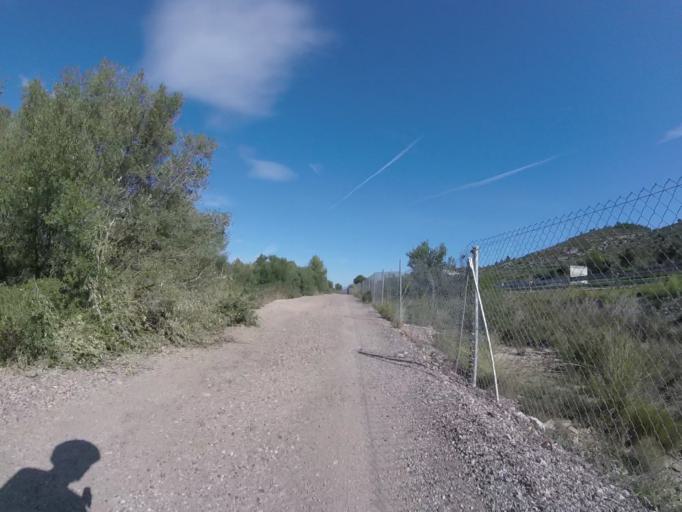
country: ES
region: Valencia
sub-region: Provincia de Castello
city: Santa Magdalena de Pulpis
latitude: 40.3811
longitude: 0.3414
